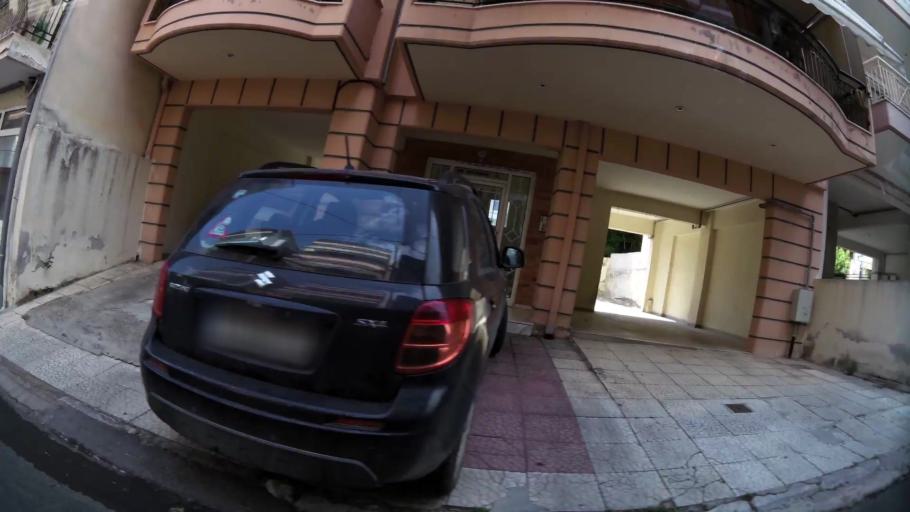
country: GR
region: Central Macedonia
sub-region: Nomos Thessalonikis
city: Polichni
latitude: 40.6607
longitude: 22.9431
